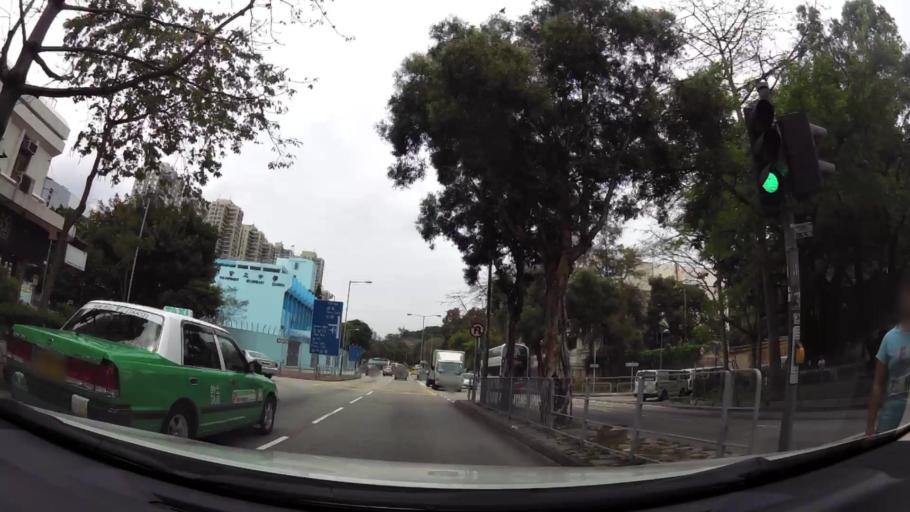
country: HK
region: Tuen Mun
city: Tuen Mun
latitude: 22.3895
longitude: 113.9802
